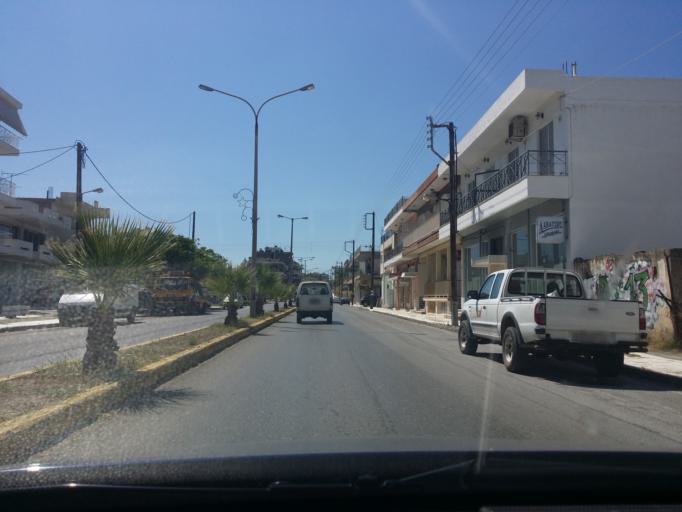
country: GR
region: Peloponnese
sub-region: Nomos Lakonias
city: Sparti
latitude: 37.0841
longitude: 22.4316
